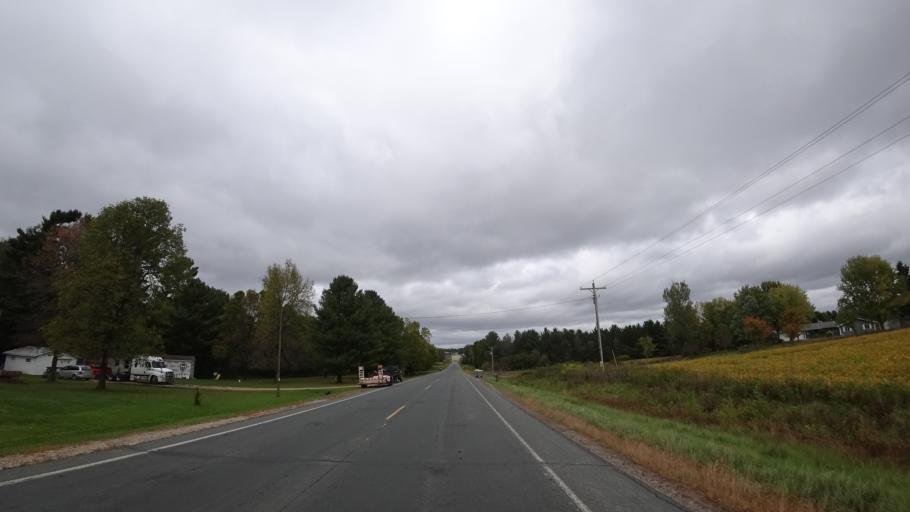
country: US
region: Wisconsin
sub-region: Saint Croix County
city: Woodville
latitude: 44.9258
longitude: -92.2782
